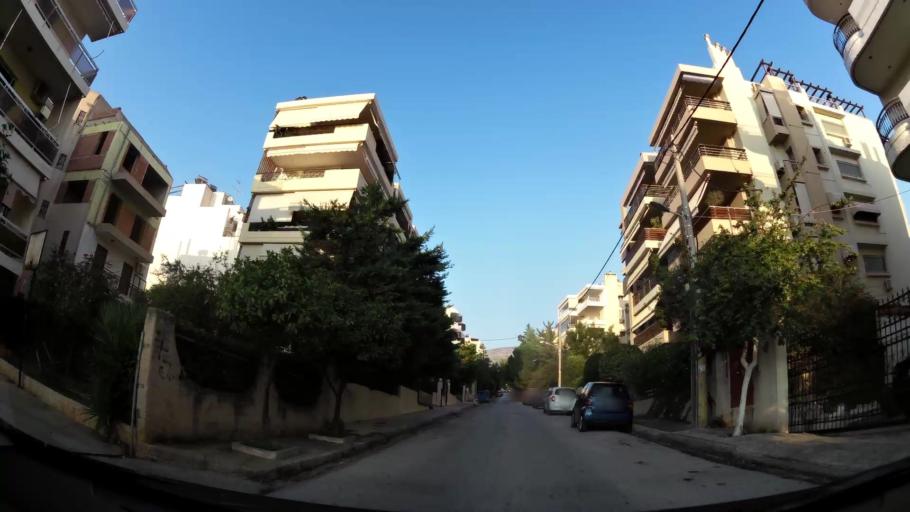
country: GR
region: Attica
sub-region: Nomarchia Athinas
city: Glyfada
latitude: 37.8850
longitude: 23.7694
